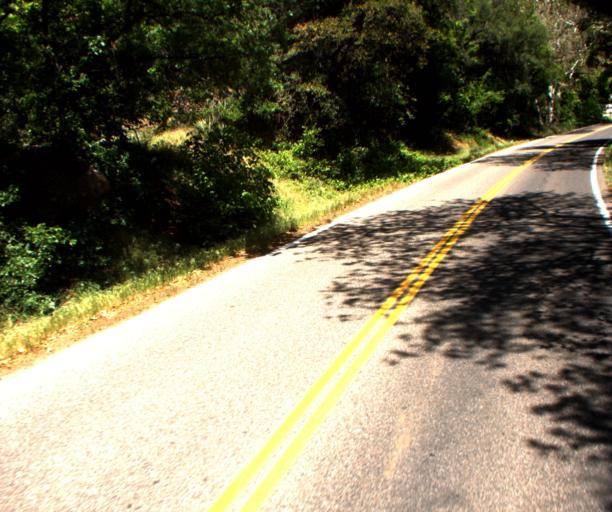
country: US
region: Arizona
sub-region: Coconino County
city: Sedona
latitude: 34.9081
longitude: -111.7287
